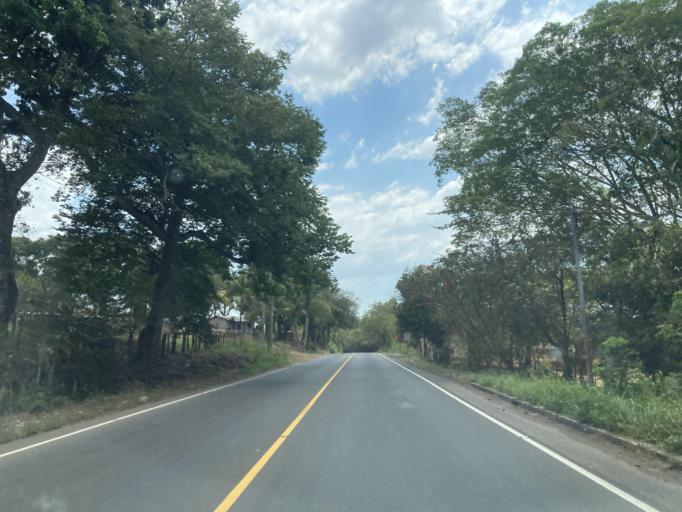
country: GT
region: Santa Rosa
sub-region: Municipio de Taxisco
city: Taxisco
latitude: 14.0770
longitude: -90.4818
